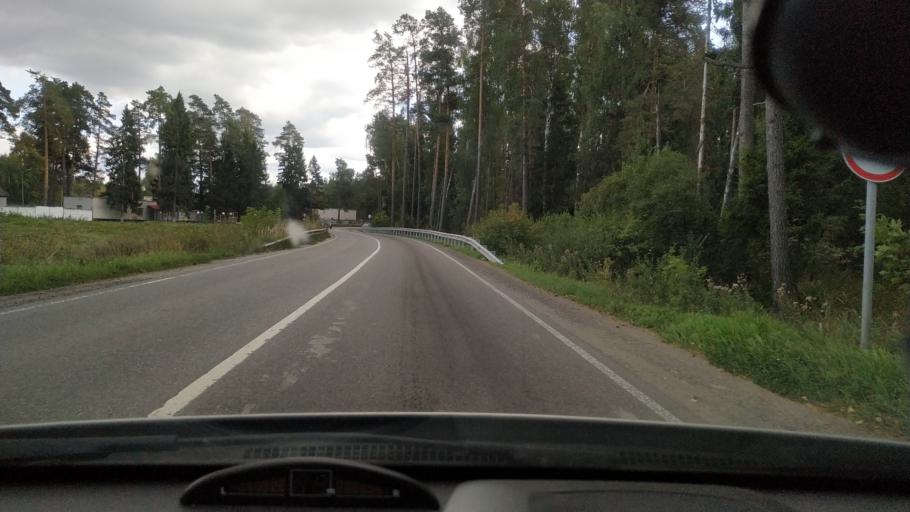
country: RU
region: Moskovskaya
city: Zheleznodorozhnyy
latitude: 55.7927
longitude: 38.0344
